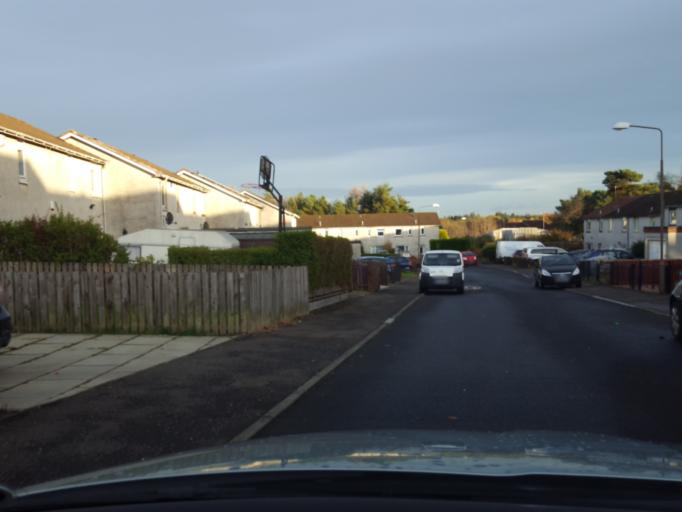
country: GB
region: Scotland
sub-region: West Lothian
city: Livingston
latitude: 55.9046
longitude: -3.5398
